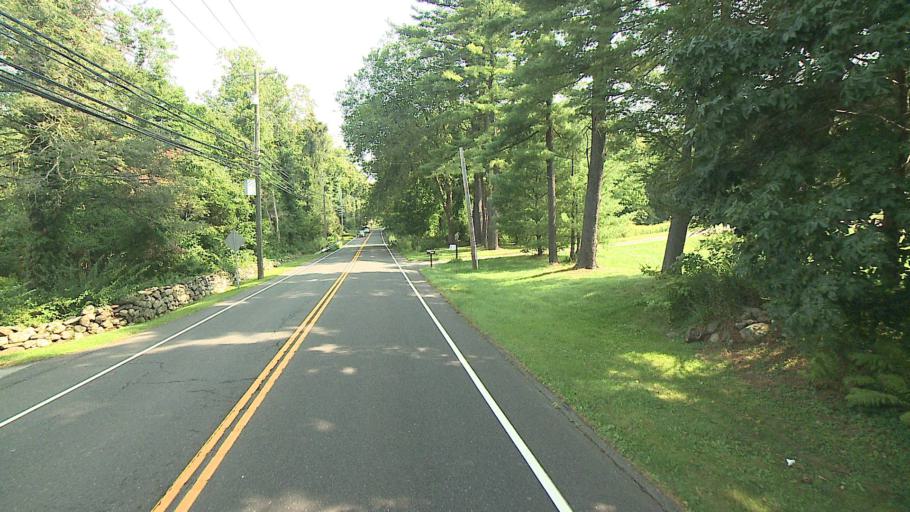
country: US
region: Connecticut
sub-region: Fairfield County
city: Georgetown
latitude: 41.2848
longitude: -73.4005
